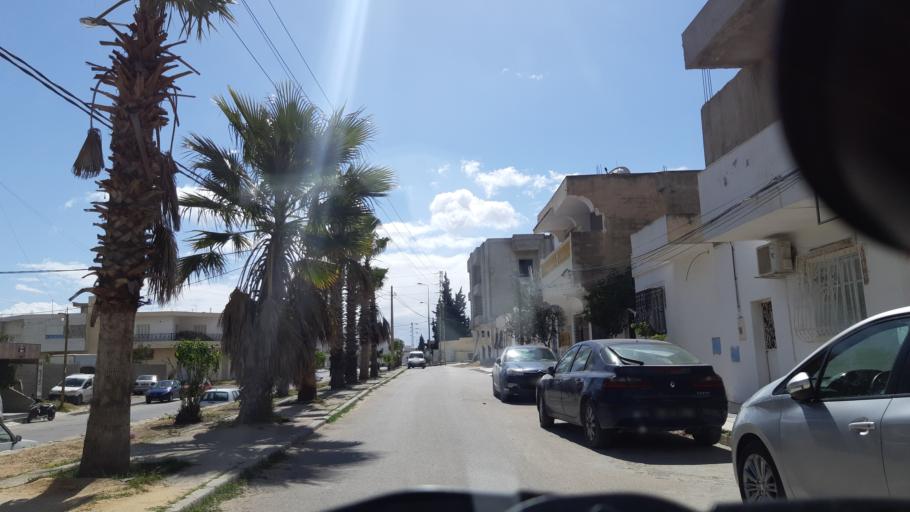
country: TN
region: Susah
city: Akouda
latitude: 35.8921
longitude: 10.5346
